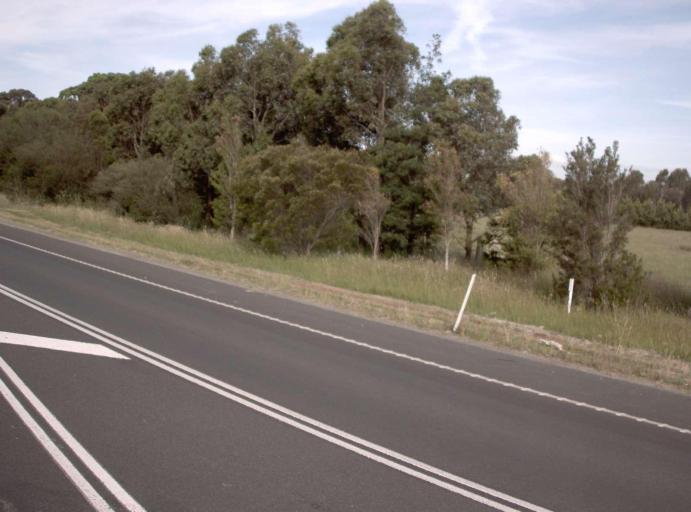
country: AU
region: Victoria
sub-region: Latrobe
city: Traralgon
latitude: -38.1297
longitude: 146.5623
